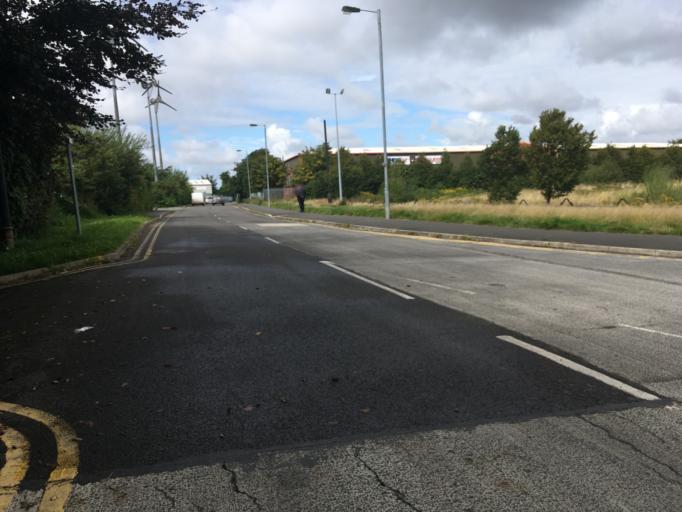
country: GB
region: England
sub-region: Sefton
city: Southport
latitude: 53.6396
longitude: -2.9686
